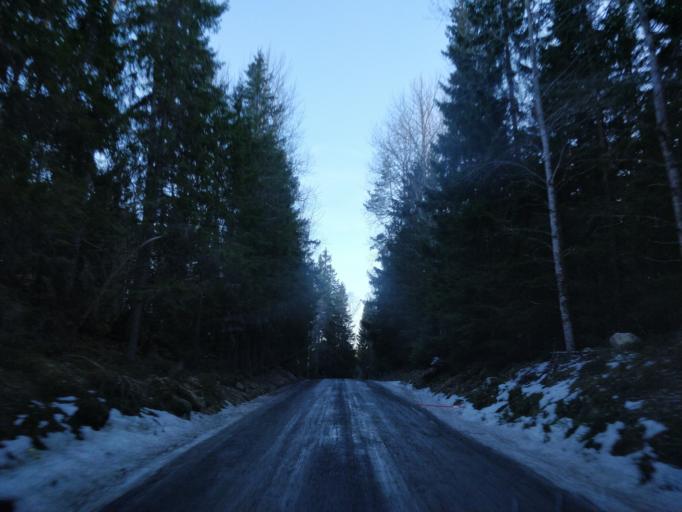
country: SE
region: Uppsala
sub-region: Enkopings Kommun
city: Orsundsbro
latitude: 59.8312
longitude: 17.1829
